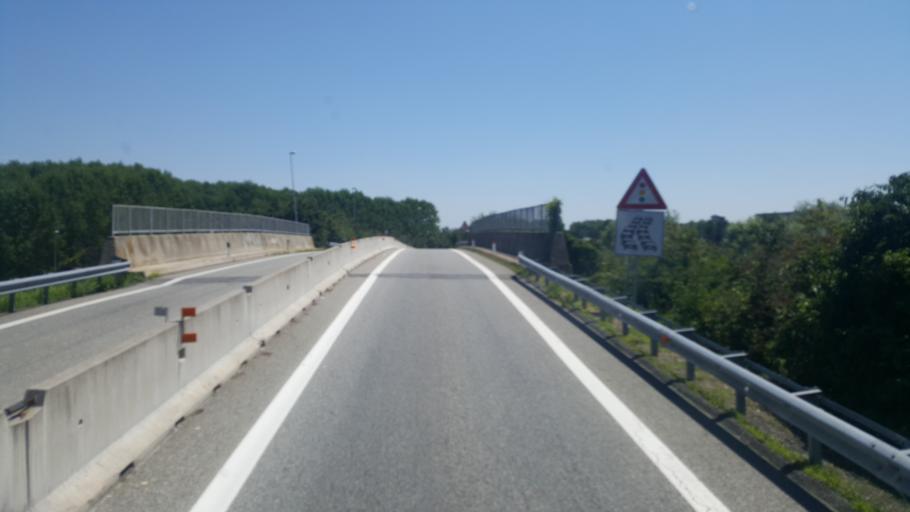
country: IT
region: Piedmont
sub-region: Provincia di Torino
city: Volvera
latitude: 44.9413
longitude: 7.5039
